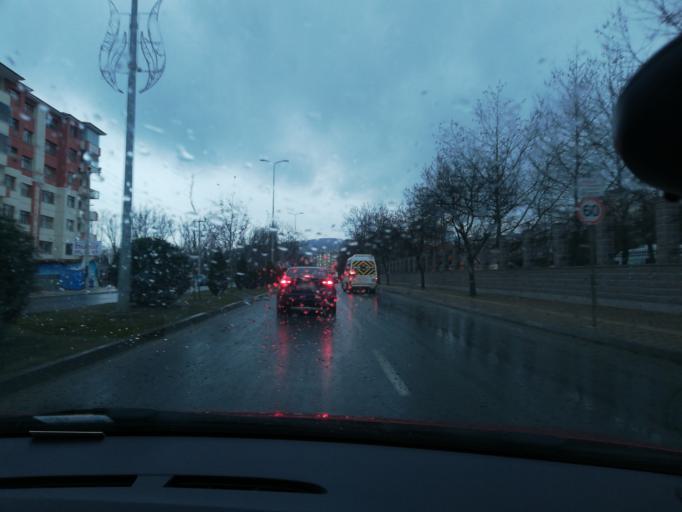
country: TR
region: Kastamonu
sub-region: Cide
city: Kastamonu
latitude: 41.4094
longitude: 33.7894
